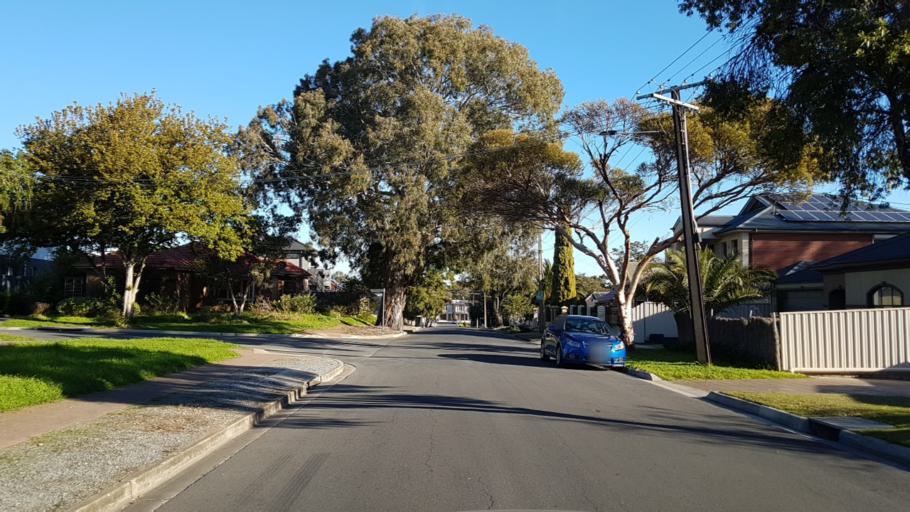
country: AU
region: South Australia
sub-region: Campbelltown
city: Campbelltown
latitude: -34.8807
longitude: 138.6593
